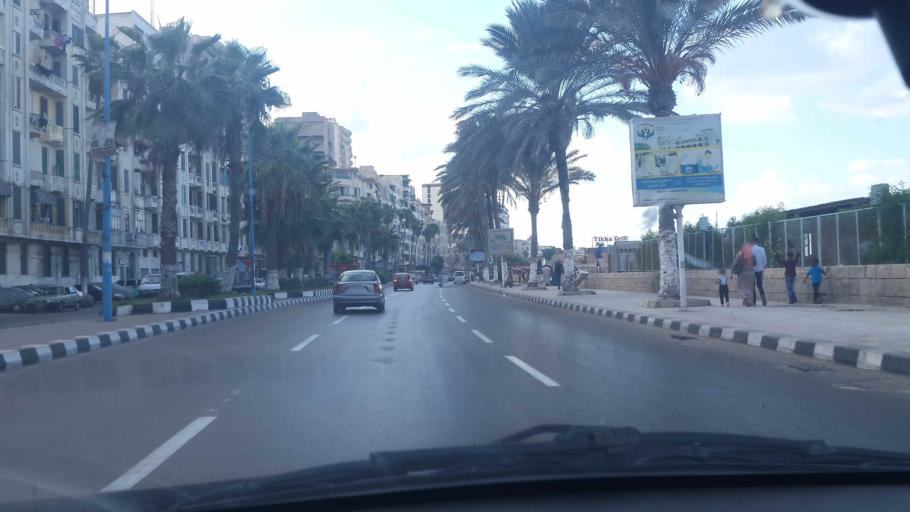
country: EG
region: Alexandria
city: Alexandria
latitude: 31.2029
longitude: 29.8866
